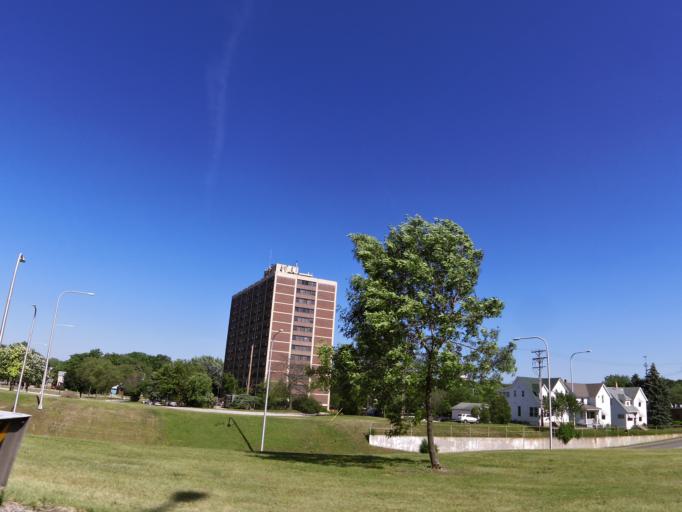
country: US
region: Illinois
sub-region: Winnebago County
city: Rockford
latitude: 42.2721
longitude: -89.0822
